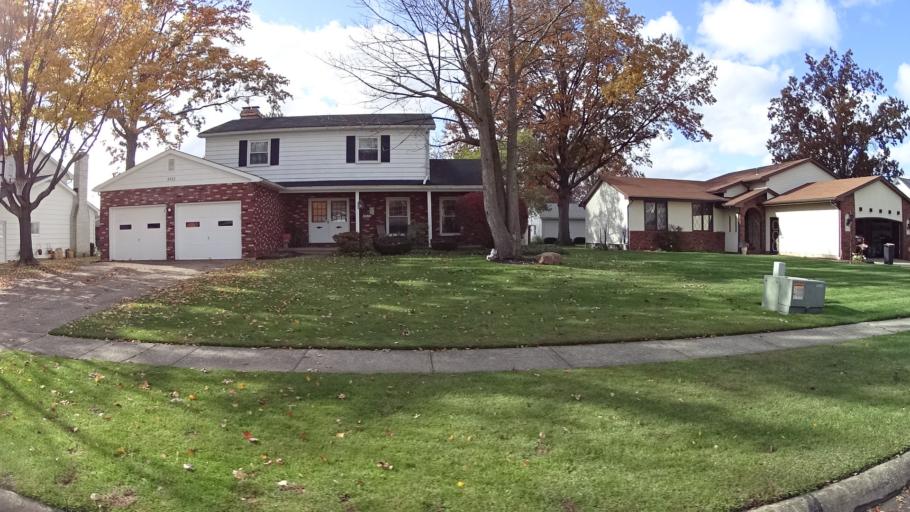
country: US
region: Ohio
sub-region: Lorain County
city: Lorain
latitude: 41.4382
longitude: -82.1933
